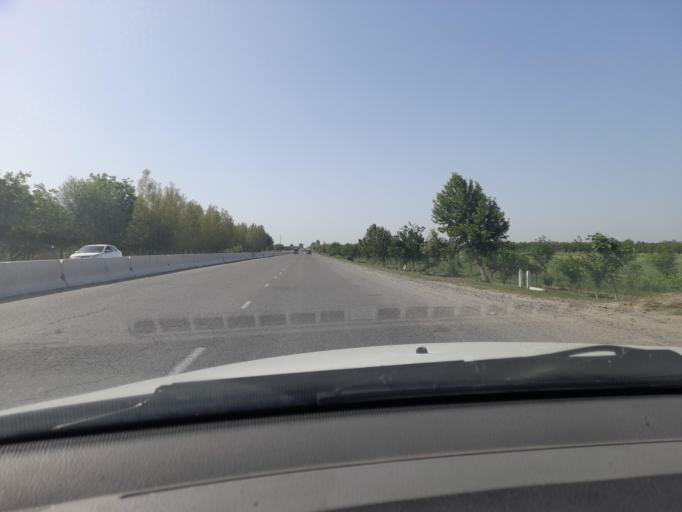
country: UZ
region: Samarqand
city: Daxbet
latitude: 39.8014
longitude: 66.8651
